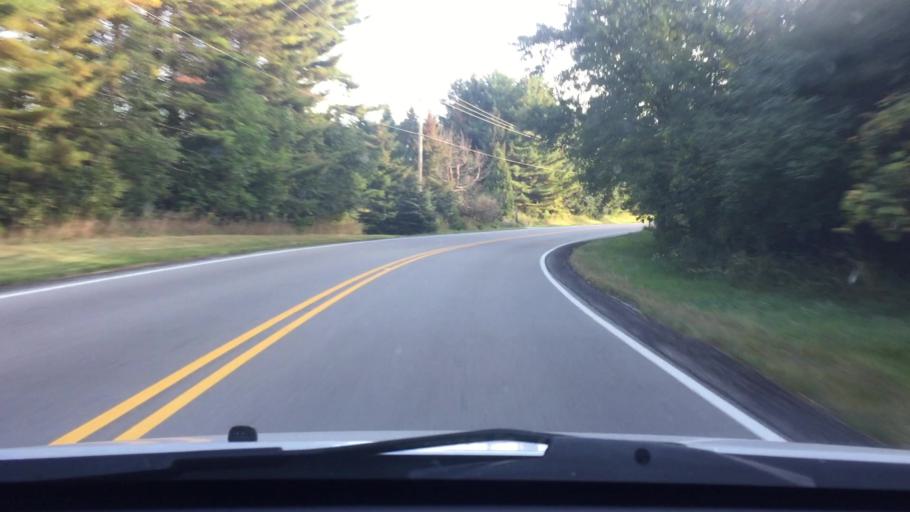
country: US
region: Wisconsin
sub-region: Waukesha County
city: Wales
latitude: 42.9842
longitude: -88.3919
